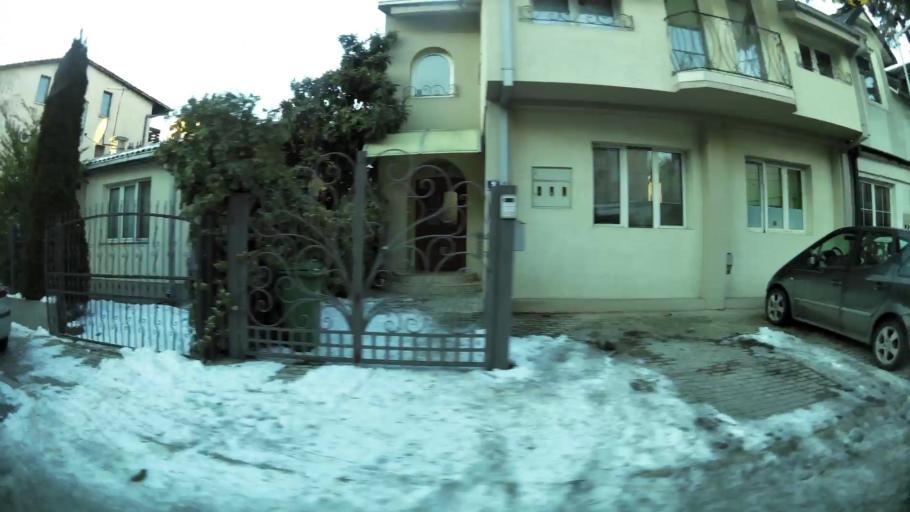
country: MK
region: Karpos
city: Skopje
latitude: 41.9938
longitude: 21.4068
